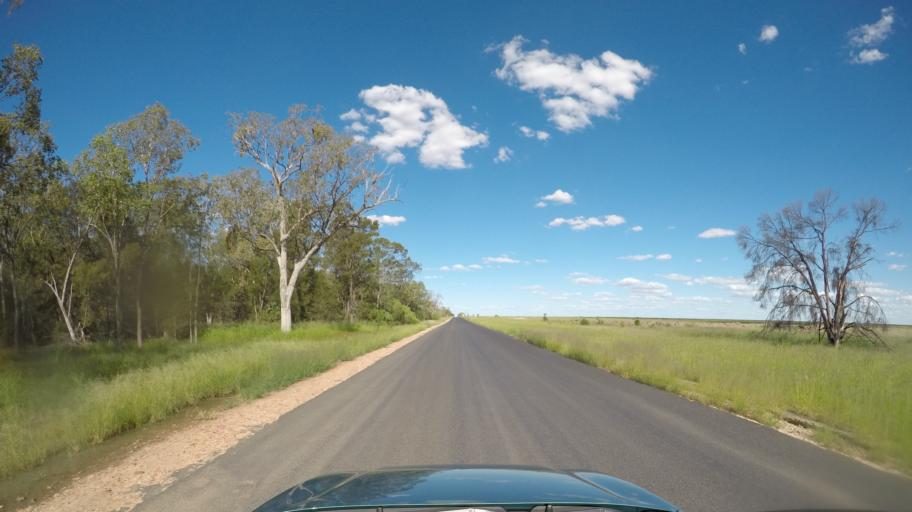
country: AU
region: Queensland
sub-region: Goondiwindi
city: Goondiwindi
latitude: -28.1460
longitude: 150.2936
